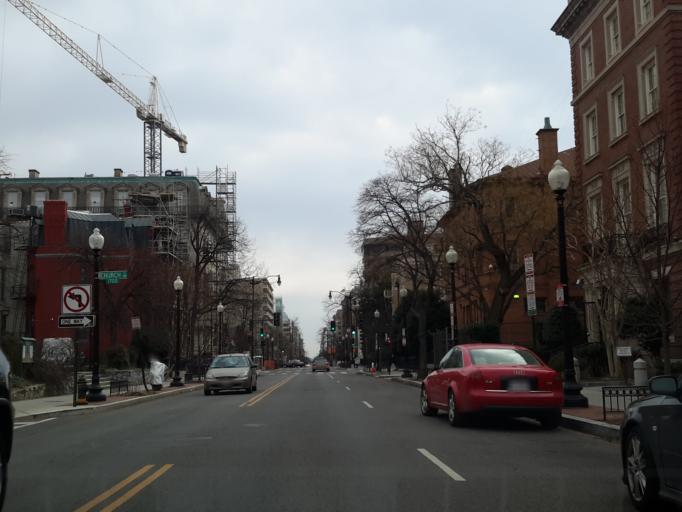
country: US
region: Washington, D.C.
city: Washington, D.C.
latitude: 38.9105
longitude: -77.0417
